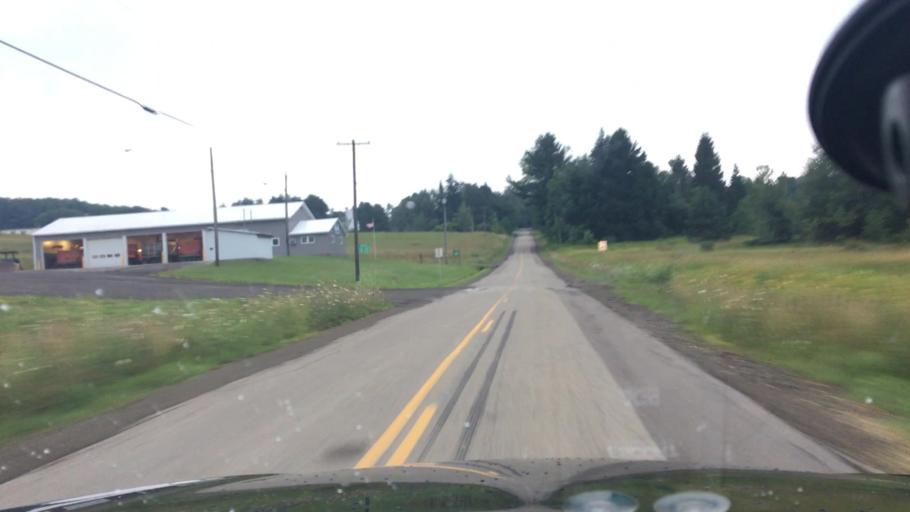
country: US
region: New York
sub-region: Cattaraugus County
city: Randolph
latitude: 42.2039
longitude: -78.8920
